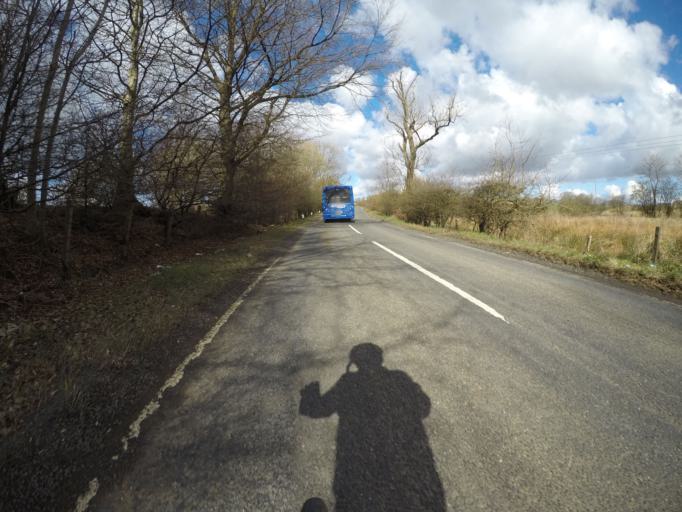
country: GB
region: Scotland
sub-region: North Ayrshire
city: Beith
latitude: 55.7338
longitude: -4.6149
